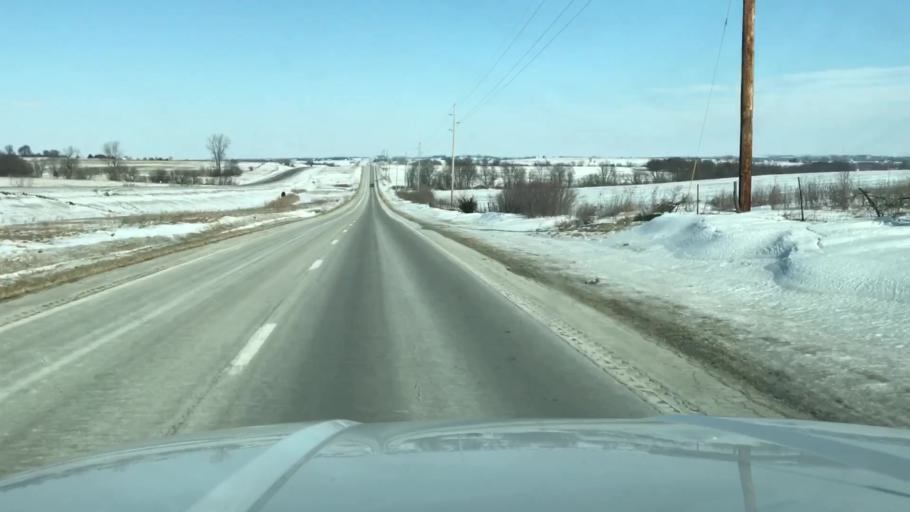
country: US
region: Missouri
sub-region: Andrew County
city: Savannah
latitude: 40.1151
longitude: -94.8697
